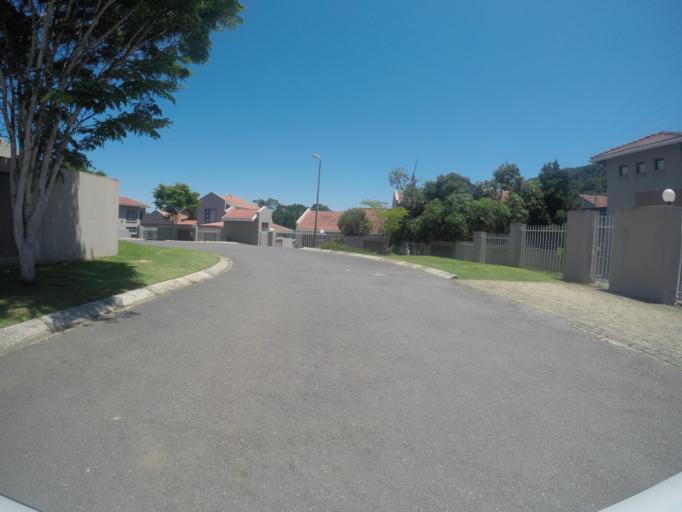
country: ZA
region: Eastern Cape
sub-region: Buffalo City Metropolitan Municipality
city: East London
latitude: -32.9275
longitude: 27.9987
